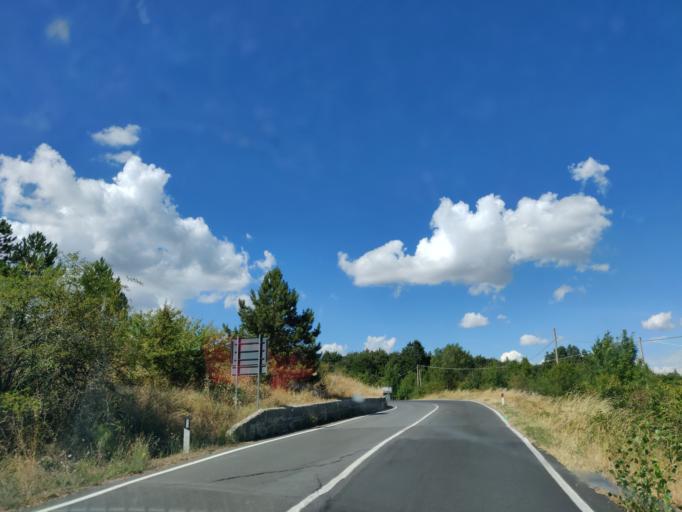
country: IT
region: Tuscany
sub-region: Provincia di Siena
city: Abbadia San Salvatore
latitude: 42.8976
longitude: 11.6686
